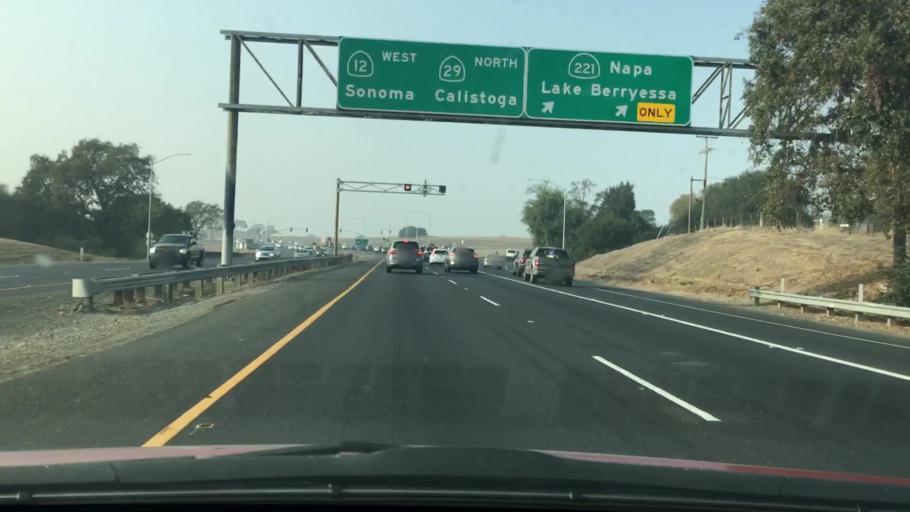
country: US
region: California
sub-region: Napa County
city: Napa
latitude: 38.2395
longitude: -122.2666
